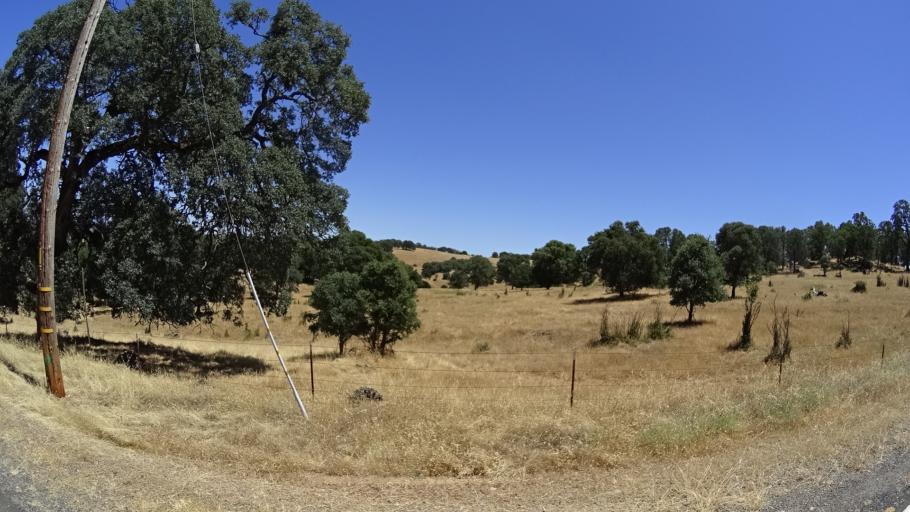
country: US
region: California
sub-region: Calaveras County
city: San Andreas
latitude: 38.0885
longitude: -120.6626
